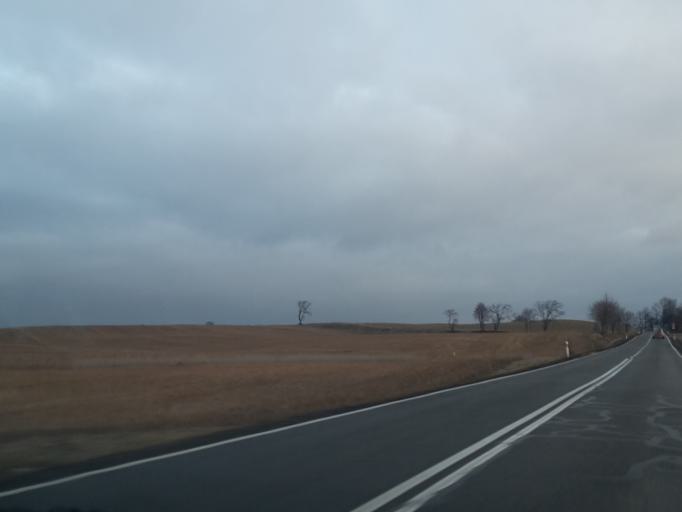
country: PL
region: Warmian-Masurian Voivodeship
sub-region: Powiat ostrodzki
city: Ostroda
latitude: 53.6445
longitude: 19.9034
